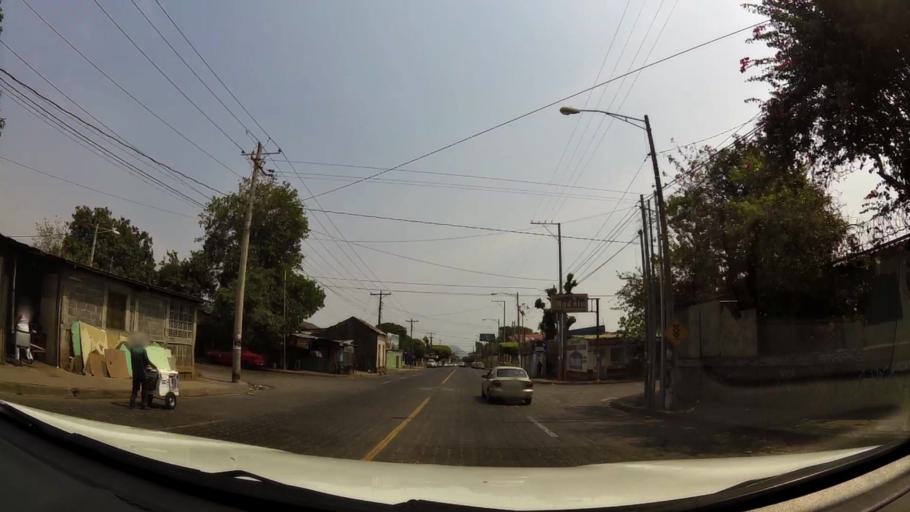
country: NI
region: Managua
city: Ciudad Sandino
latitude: 12.1477
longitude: -86.2975
